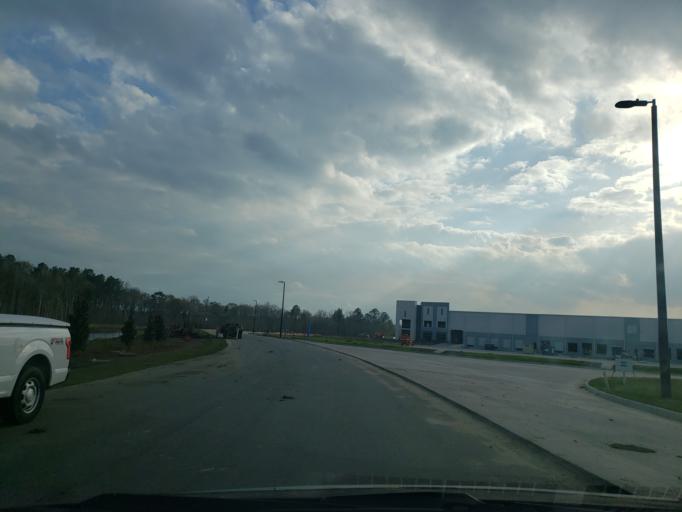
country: US
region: Georgia
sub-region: Effingham County
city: Rincon
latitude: 32.2325
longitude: -81.2087
